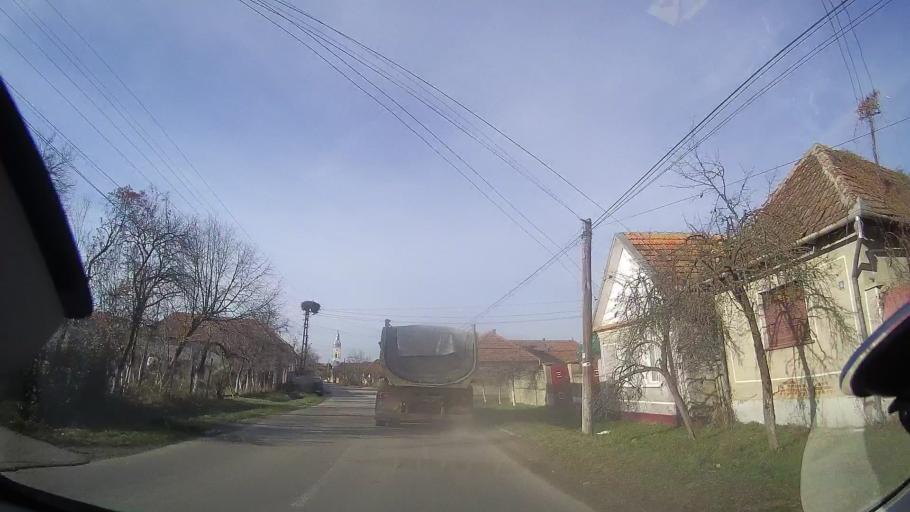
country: RO
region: Bihor
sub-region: Comuna Brusturi
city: Brusturi
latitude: 47.1420
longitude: 22.2642
